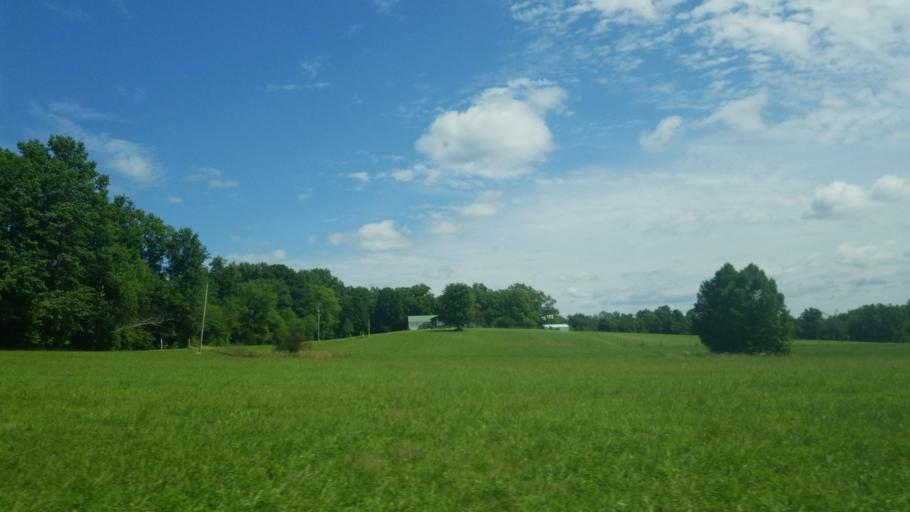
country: US
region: Illinois
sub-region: Williamson County
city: Johnston City
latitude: 37.7789
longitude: -88.8130
